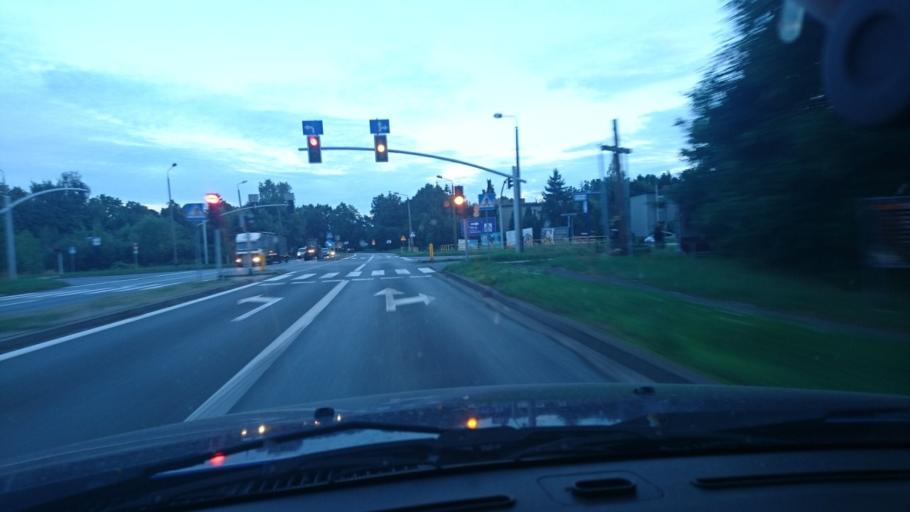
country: PL
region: Silesian Voivodeship
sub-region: Powiat tarnogorski
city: Tarnowskie Gory
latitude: 50.4428
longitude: 18.8355
